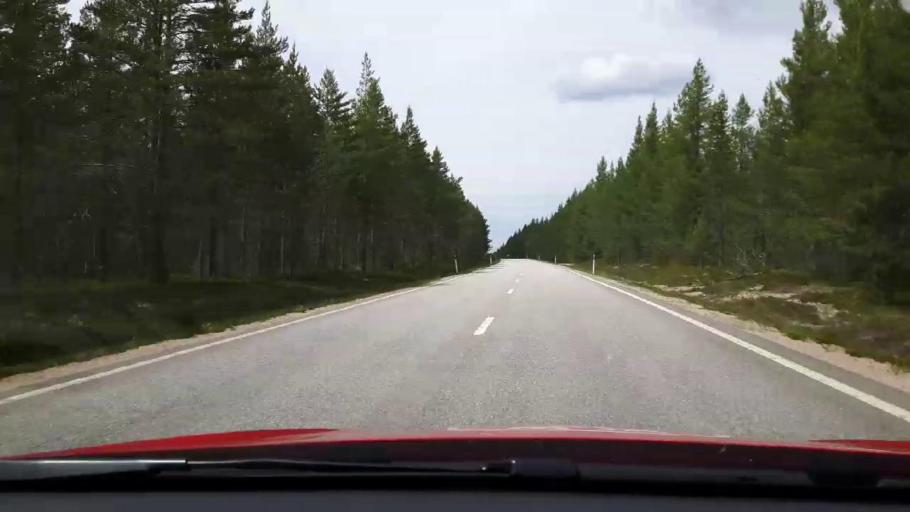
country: SE
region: Jaemtland
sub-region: Harjedalens Kommun
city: Sveg
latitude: 62.0586
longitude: 14.2936
